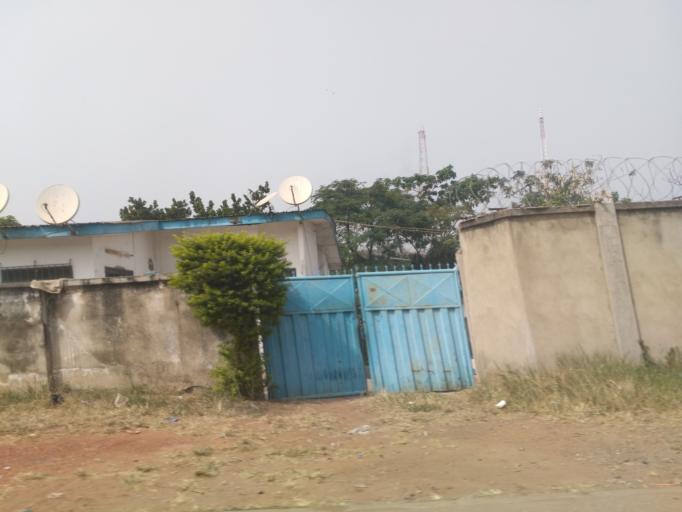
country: GH
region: Ashanti
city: Kumasi
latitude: 6.6787
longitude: -1.6070
